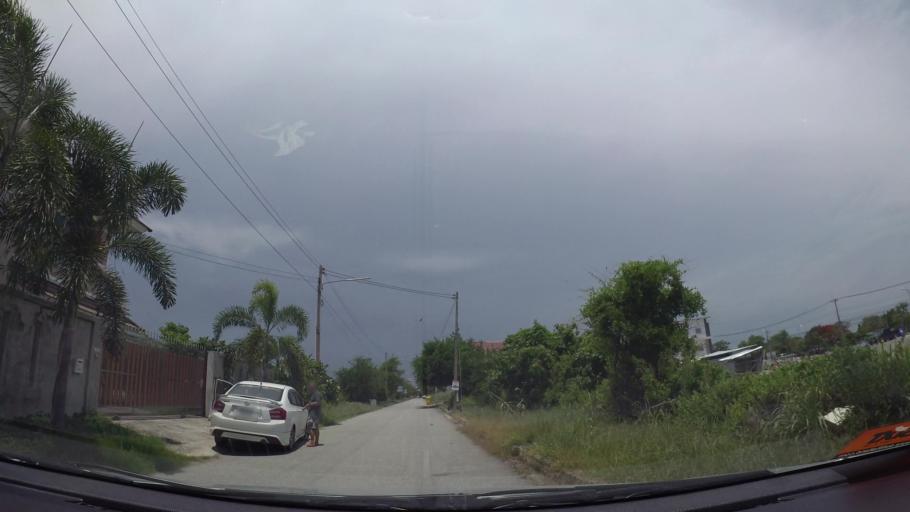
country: TH
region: Chon Buri
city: Chon Buri
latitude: 13.3422
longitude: 100.9509
